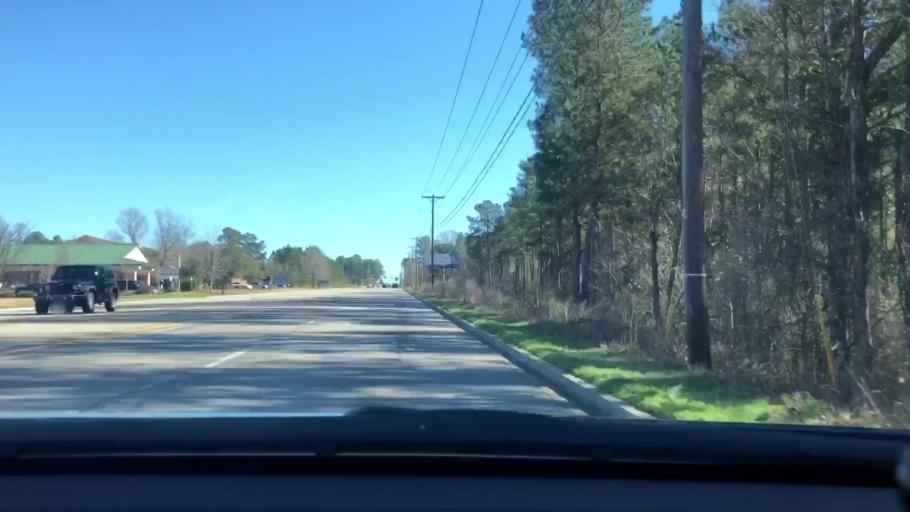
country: US
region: South Carolina
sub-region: Lexington County
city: Oak Grove
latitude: 34.0133
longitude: -81.1664
